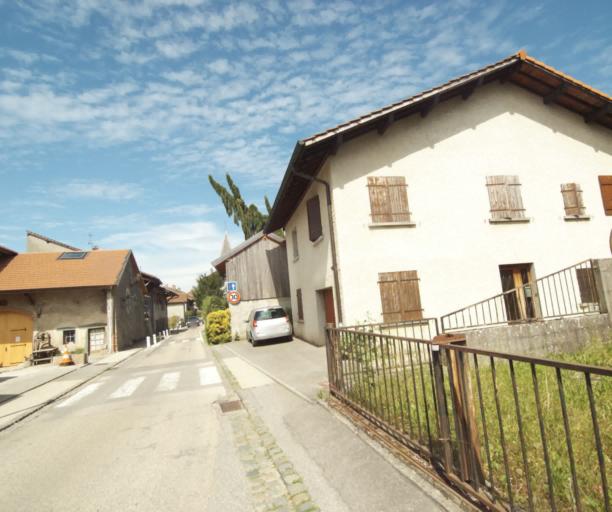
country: FR
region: Rhone-Alpes
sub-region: Departement de la Haute-Savoie
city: Bons-en-Chablais
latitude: 46.2754
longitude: 6.4113
